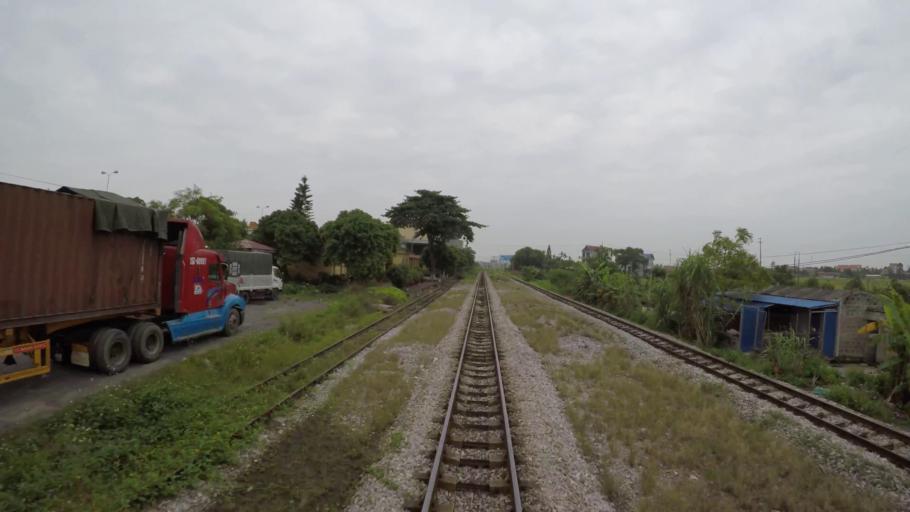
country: VN
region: Hai Duong
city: Phu Thai
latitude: 20.9330
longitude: 106.5520
